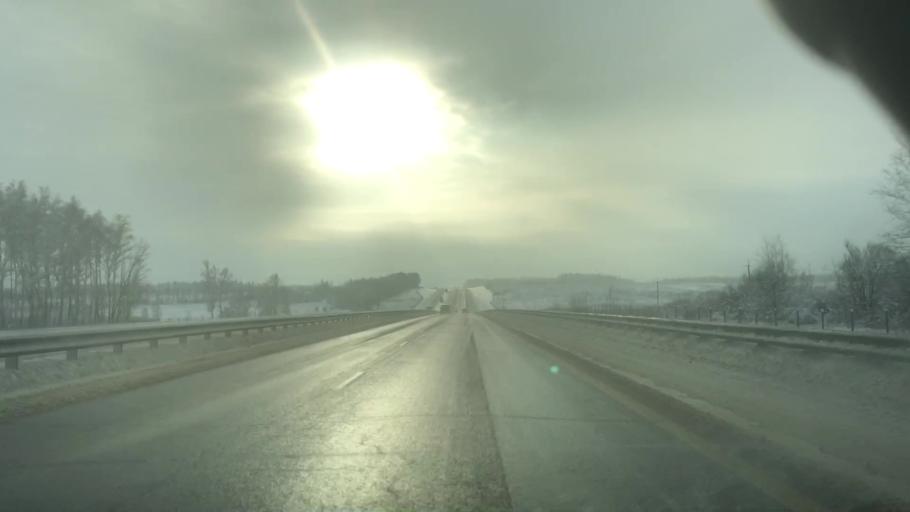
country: RU
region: Tula
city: Venev
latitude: 54.3230
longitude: 38.1543
